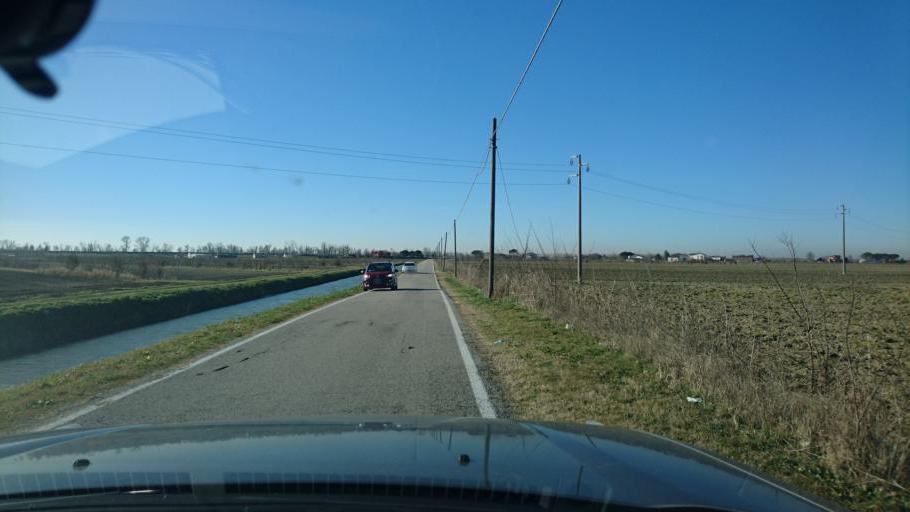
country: IT
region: Emilia-Romagna
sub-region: Provincia di Ferrara
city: Mesola
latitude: 44.9343
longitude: 12.2132
